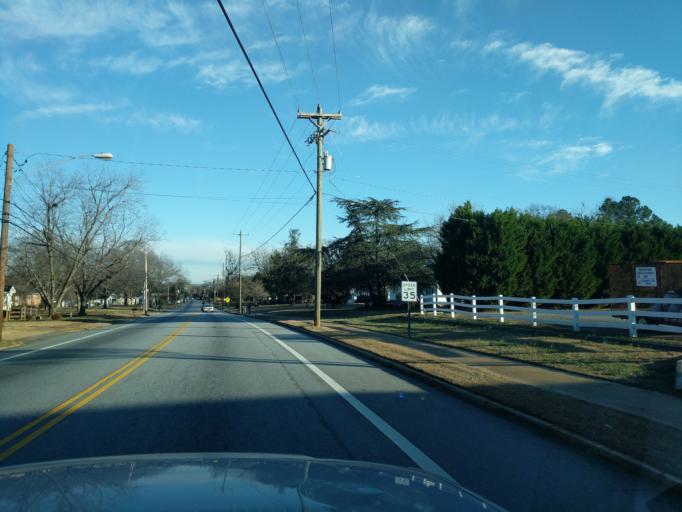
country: US
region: South Carolina
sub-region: Anderson County
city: Williamston
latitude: 34.6478
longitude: -82.4821
